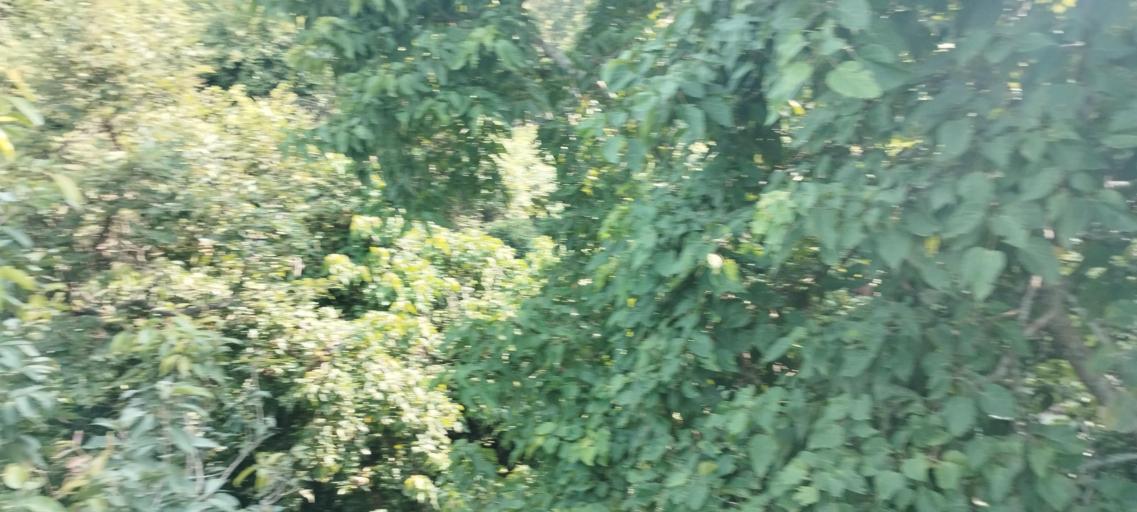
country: NP
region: Far Western
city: Tikapur
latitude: 28.4786
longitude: 81.2405
